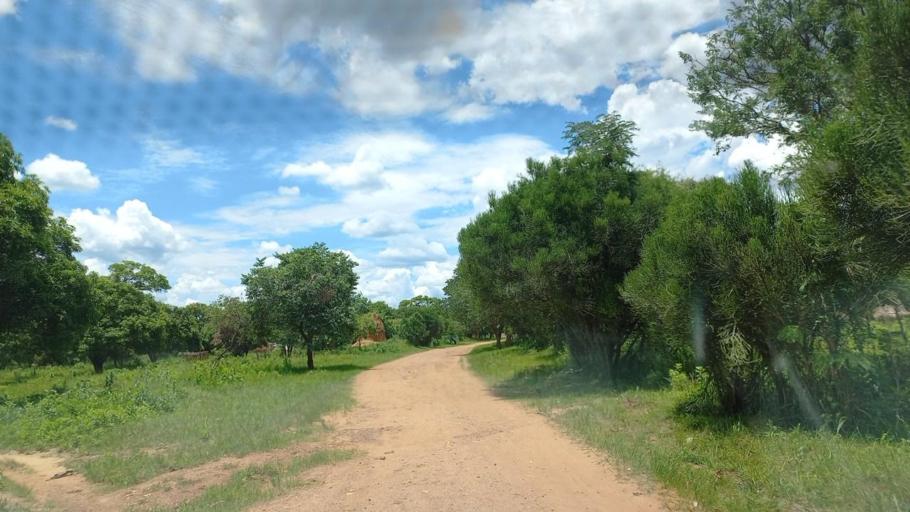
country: ZM
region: North-Western
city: Mwinilunga
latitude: -12.5468
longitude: 24.2033
